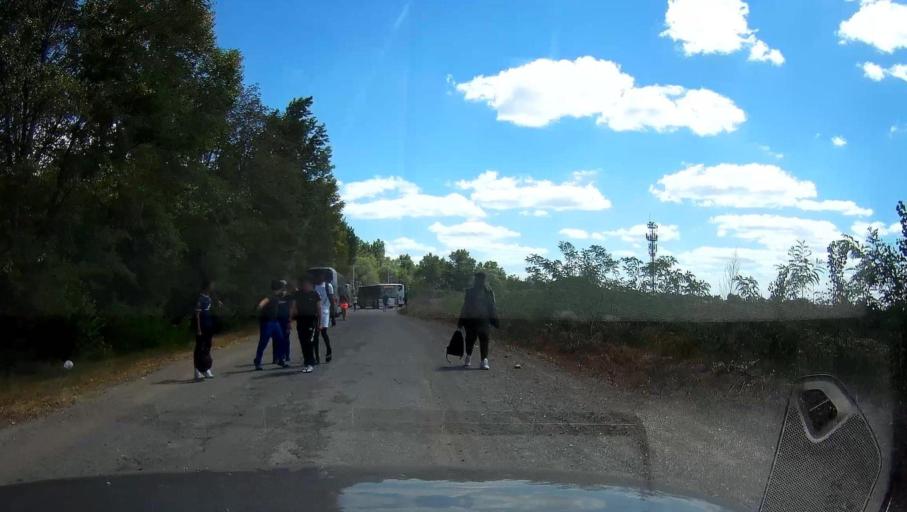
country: FR
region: Rhone-Alpes
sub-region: Departement du Rhone
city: Anse
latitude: 45.9441
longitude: 4.7216
